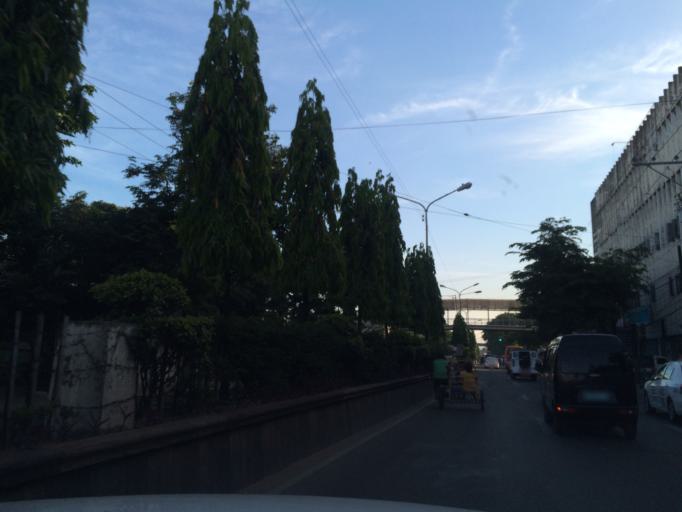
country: PH
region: Central Visayas
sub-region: Cebu City
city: Calero
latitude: 10.2960
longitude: 123.8841
